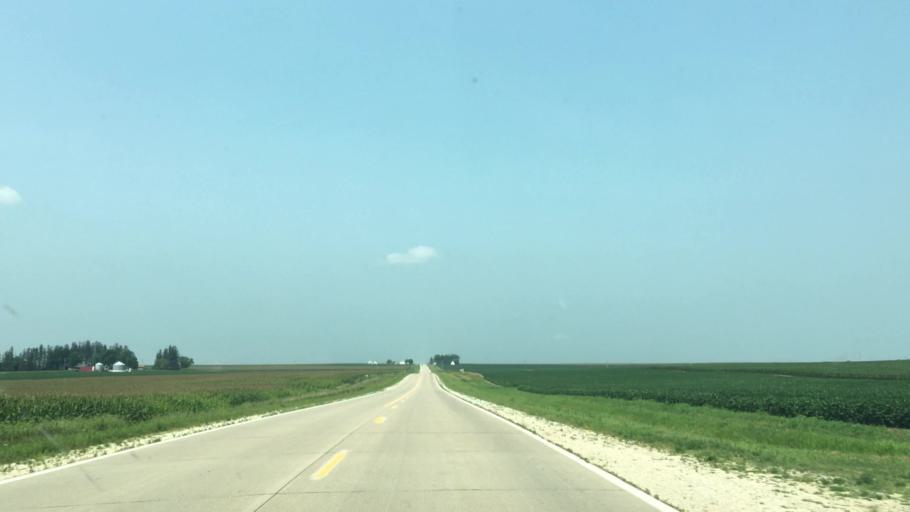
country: US
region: Iowa
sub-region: Fayette County
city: Oelwein
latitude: 42.6948
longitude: -91.8050
